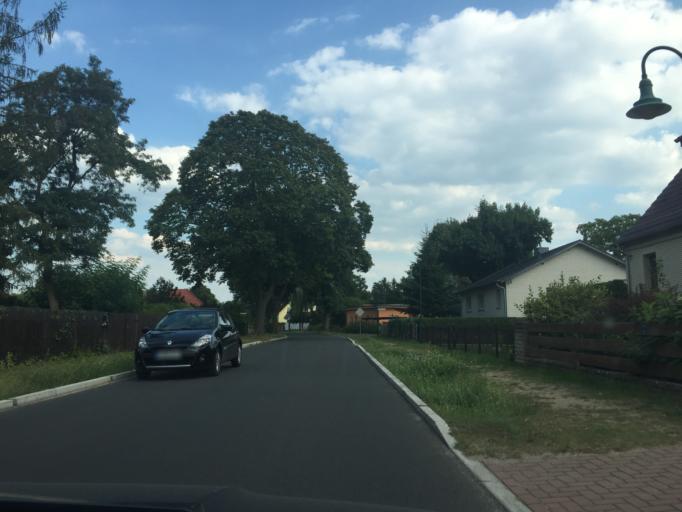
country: DE
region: Brandenburg
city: Erkner
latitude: 52.3839
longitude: 13.7669
